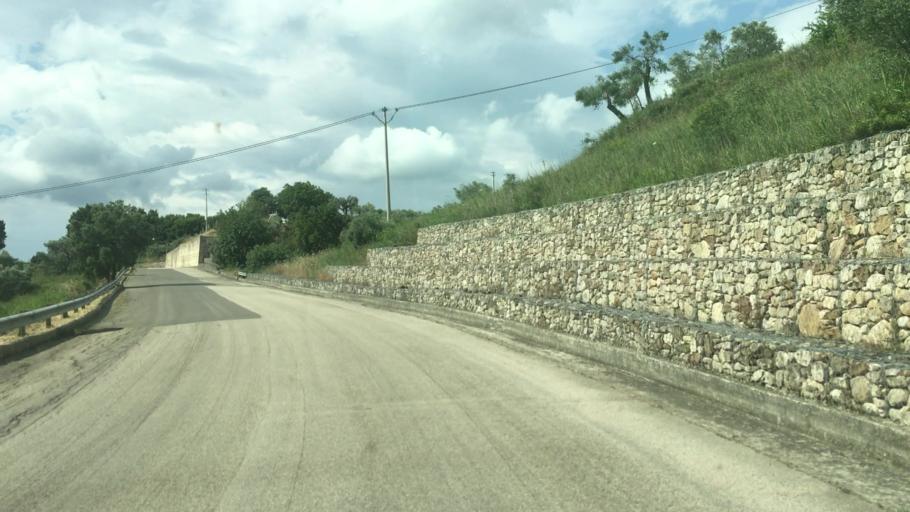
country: IT
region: Basilicate
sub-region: Provincia di Matera
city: San Mauro Forte
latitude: 40.4813
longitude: 16.2668
